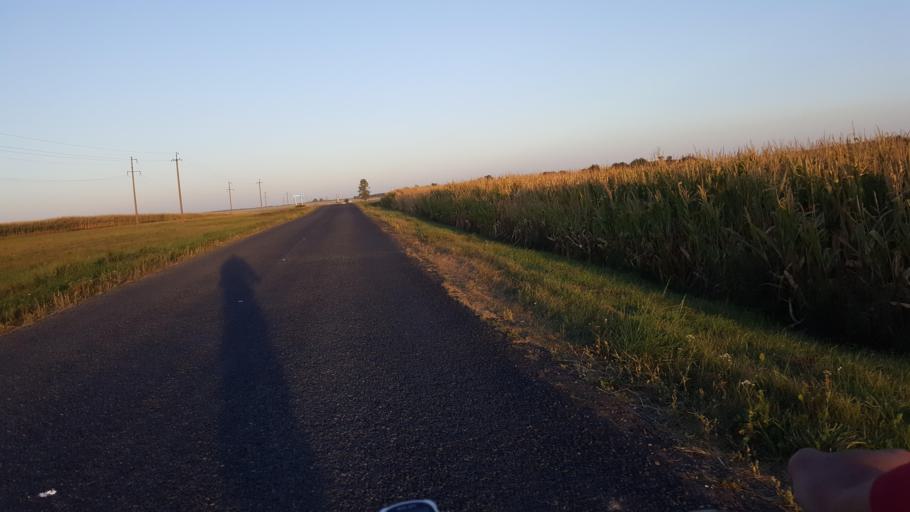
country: BY
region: Brest
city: Charnawchytsy
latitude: 52.2899
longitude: 23.5710
